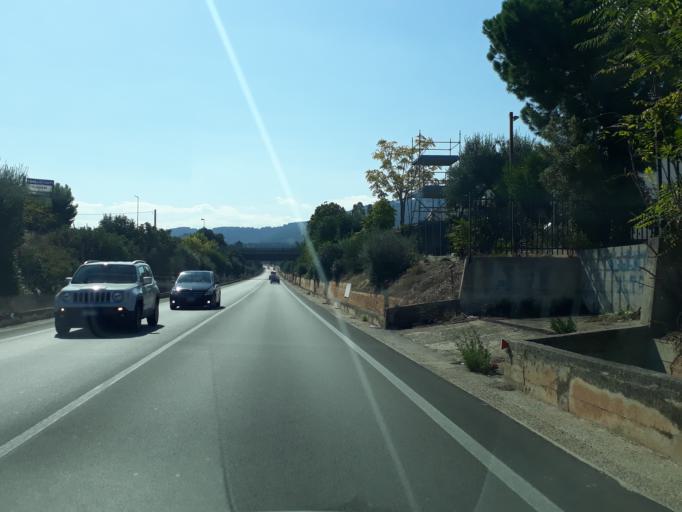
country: IT
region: Apulia
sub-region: Provincia di Brindisi
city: Fasano
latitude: 40.8430
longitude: 17.3536
